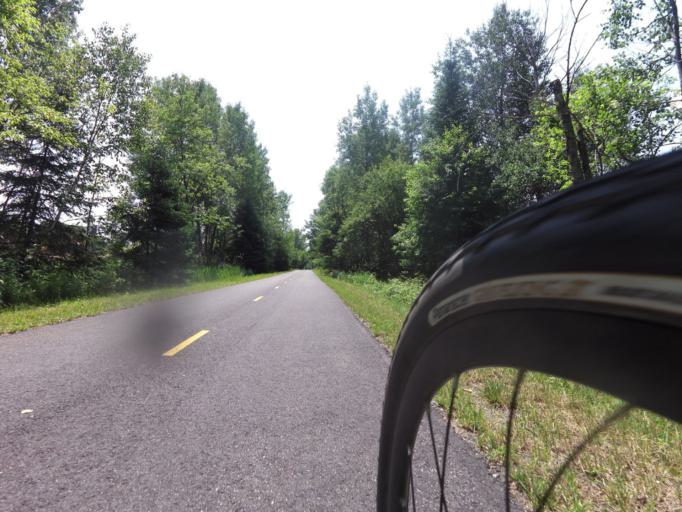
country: CA
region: Quebec
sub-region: Laurentides
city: Mont-Tremblant
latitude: 46.1400
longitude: -74.5958
